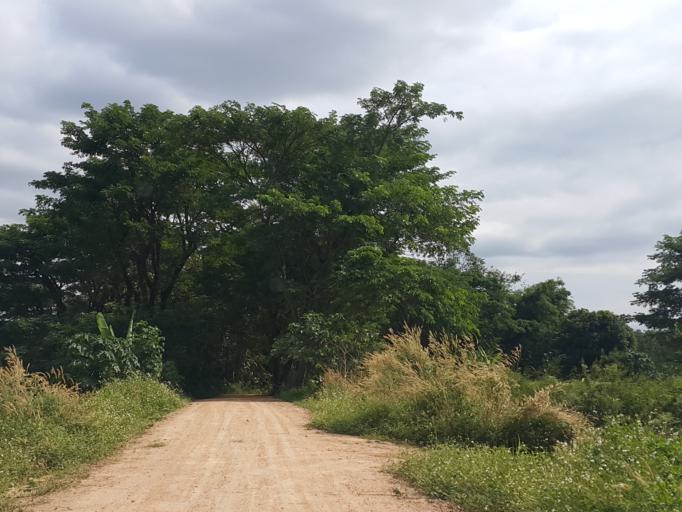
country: TH
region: Lampang
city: Hang Chat
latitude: 18.4874
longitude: 99.4000
